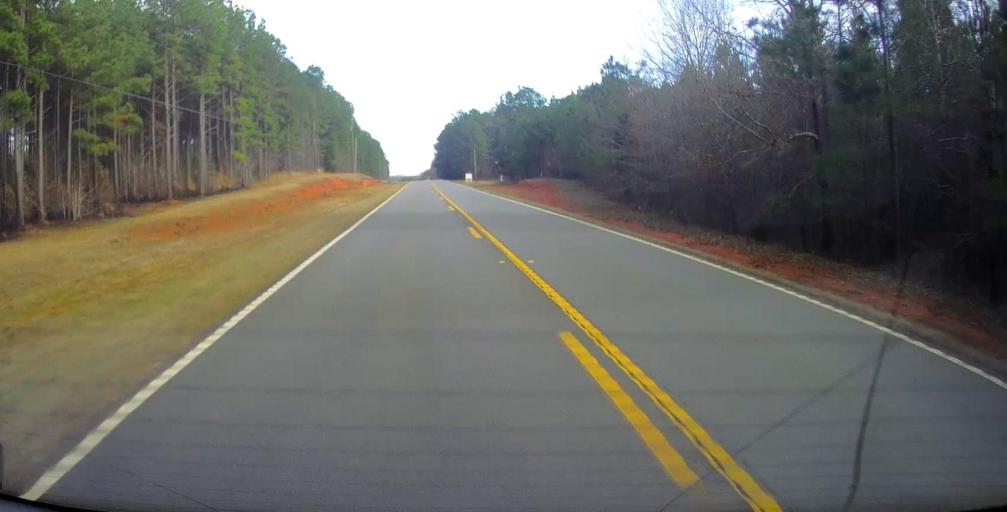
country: US
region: Georgia
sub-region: Harris County
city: Hamilton
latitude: 32.6892
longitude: -84.7844
